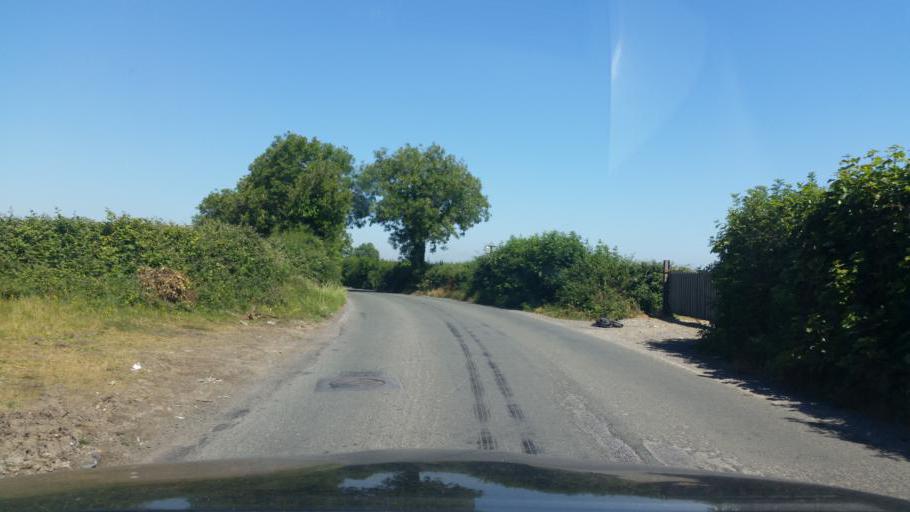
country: IE
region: Leinster
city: Ballymun
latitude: 53.4407
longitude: -6.2931
